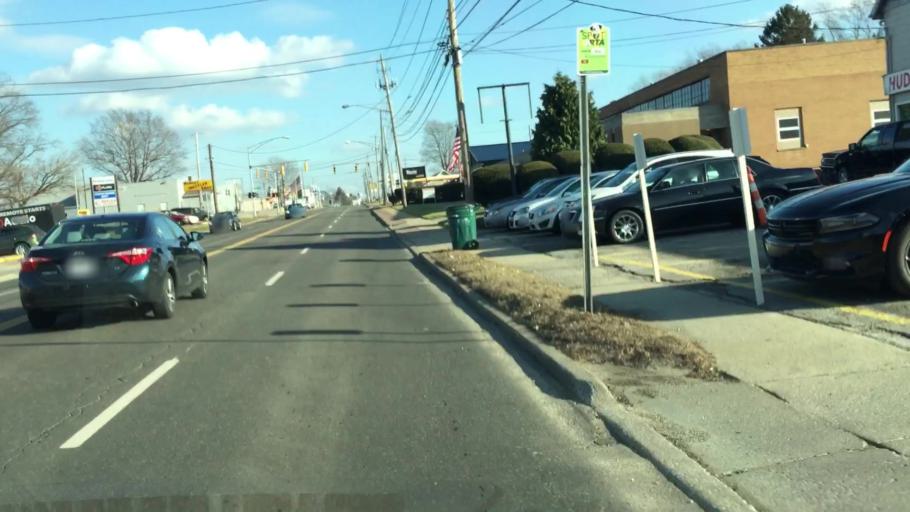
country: US
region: Ohio
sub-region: Portage County
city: Kent
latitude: 41.1518
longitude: -81.3867
